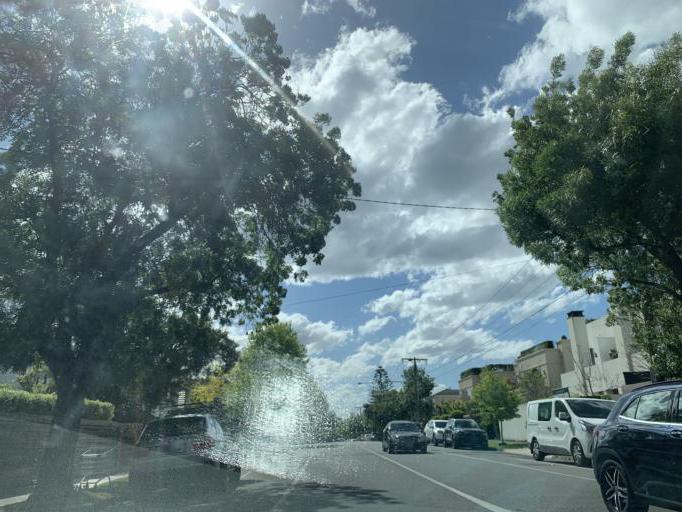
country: AU
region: Victoria
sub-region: Bayside
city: North Brighton
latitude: -37.9148
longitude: 144.9935
